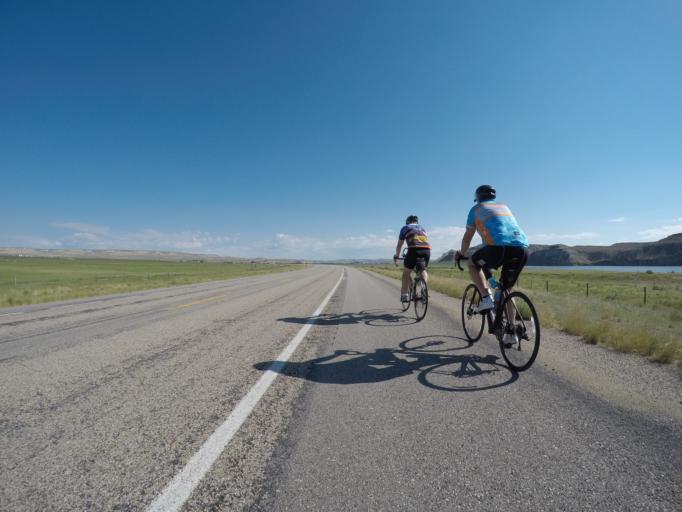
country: US
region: Wyoming
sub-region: Sublette County
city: Marbleton
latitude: 42.1405
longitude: -110.1851
